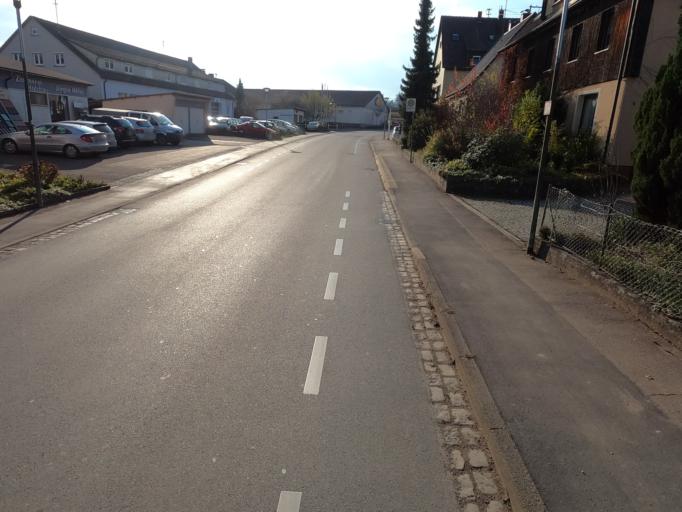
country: DE
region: Baden-Wuerttemberg
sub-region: Regierungsbezirk Stuttgart
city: Hattenhofen
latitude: 48.6675
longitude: 9.5766
